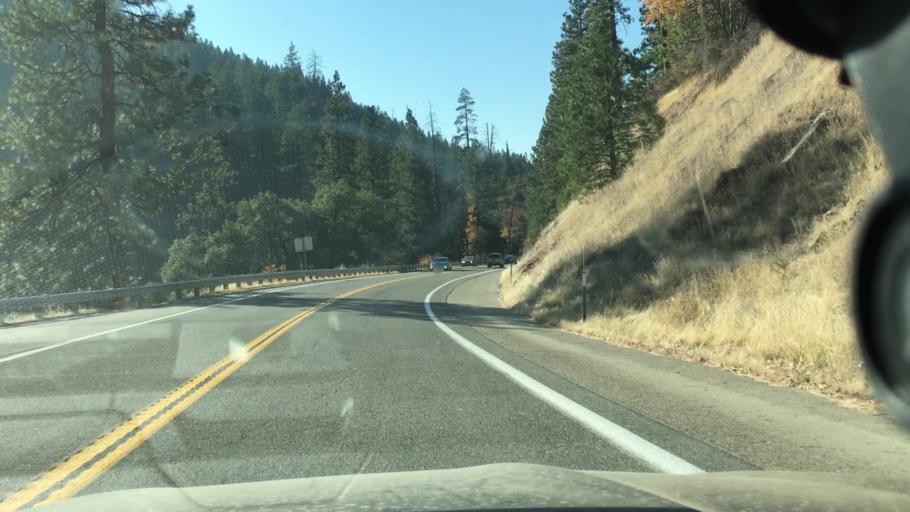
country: US
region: California
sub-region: El Dorado County
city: Pollock Pines
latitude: 38.7753
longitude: -120.4148
